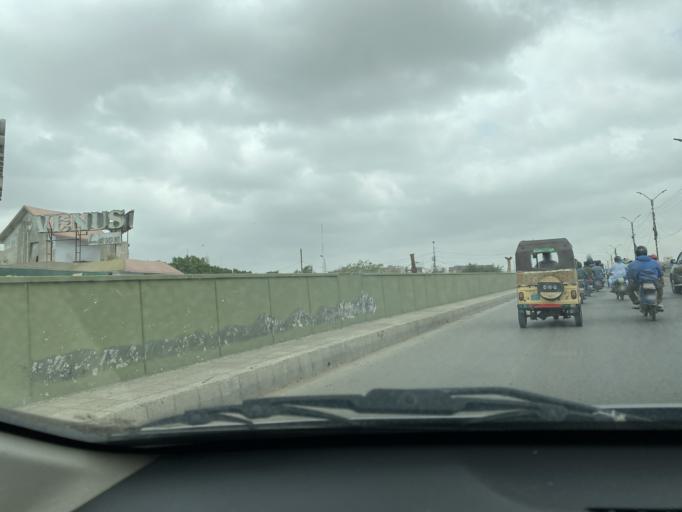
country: PK
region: Sindh
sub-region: Karachi District
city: Karachi
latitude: 24.8649
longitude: 67.0849
